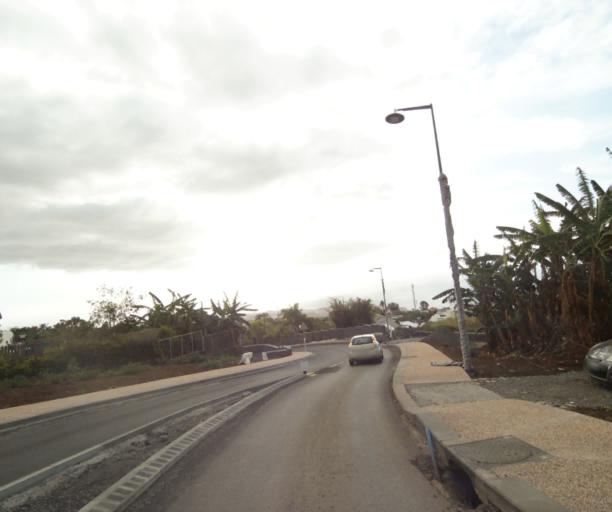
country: RE
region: Reunion
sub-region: Reunion
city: Saint-Paul
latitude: -21.0370
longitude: 55.2974
